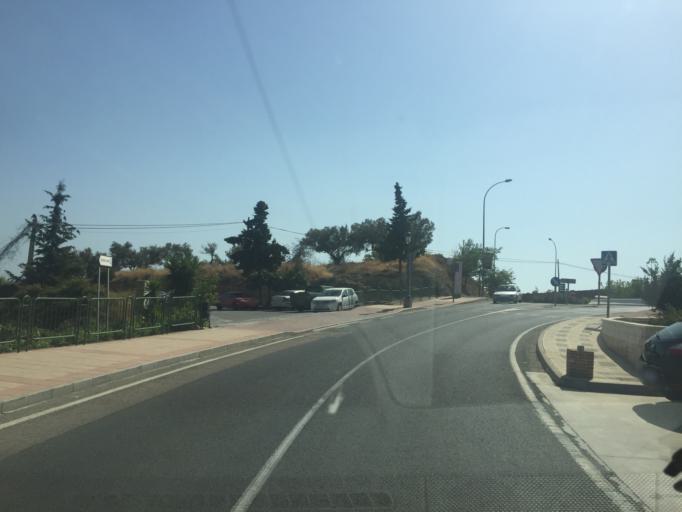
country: ES
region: Andalusia
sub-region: Provincia de Malaga
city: Nerja
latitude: 36.7592
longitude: -3.8458
